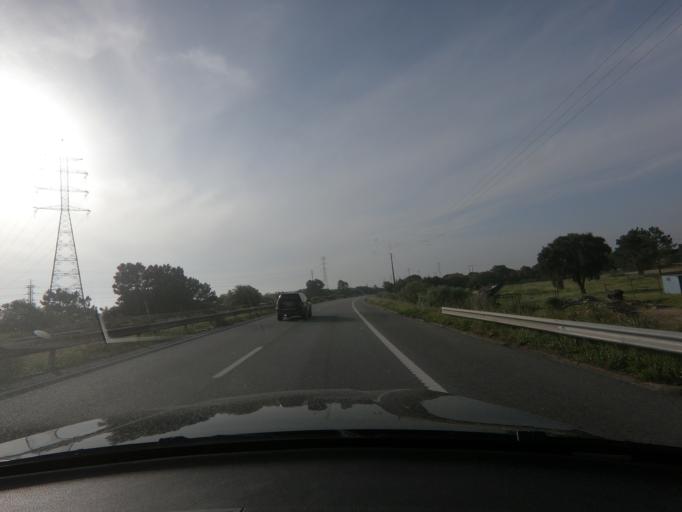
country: PT
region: Setubal
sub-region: Palmela
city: Palmela
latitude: 38.5800
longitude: -8.8703
